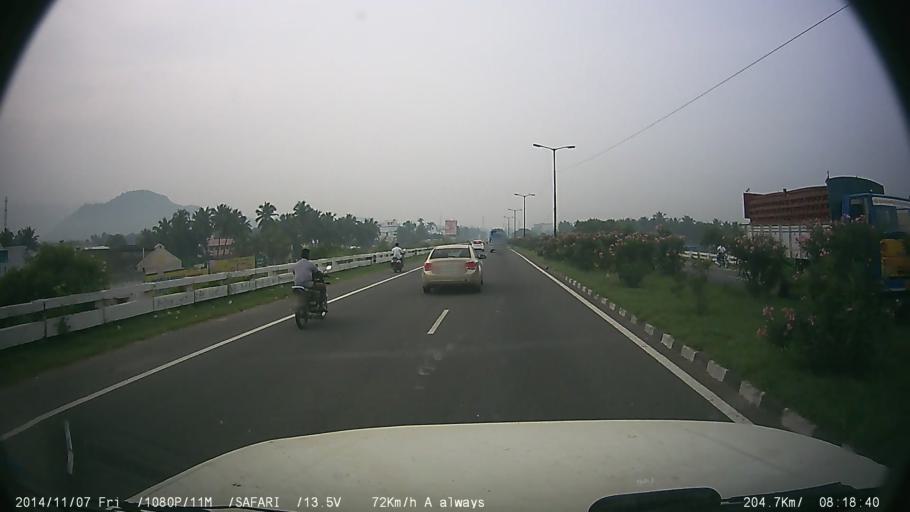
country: IN
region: Tamil Nadu
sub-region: Salem
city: Salem
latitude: 11.6579
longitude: 78.1216
